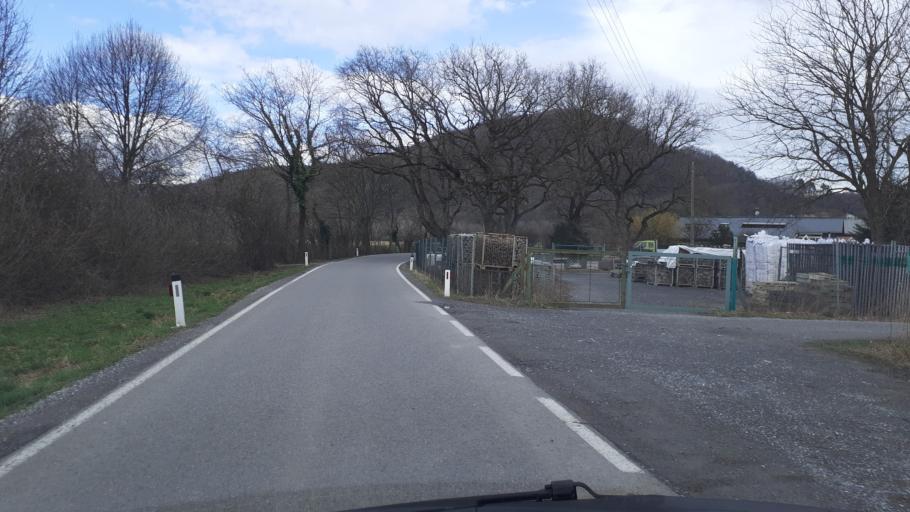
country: AT
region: Vorarlberg
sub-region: Politischer Bezirk Feldkirch
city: Koblach
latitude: 47.3219
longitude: 9.6160
